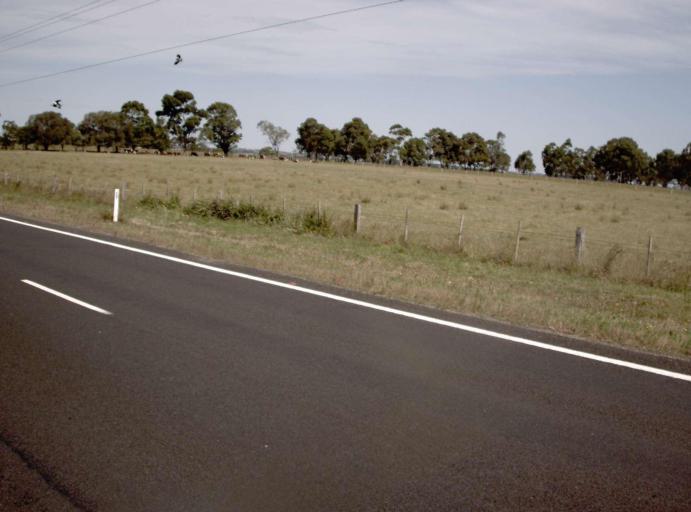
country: AU
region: Victoria
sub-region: East Gippsland
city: Bairnsdale
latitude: -37.8216
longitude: 147.7849
